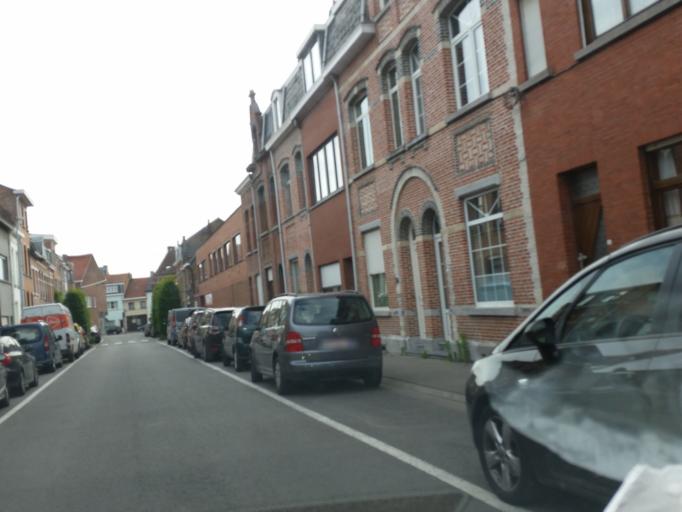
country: BE
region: Flanders
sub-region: Provincie Antwerpen
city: Mechelen
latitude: 51.0120
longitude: 4.4851
